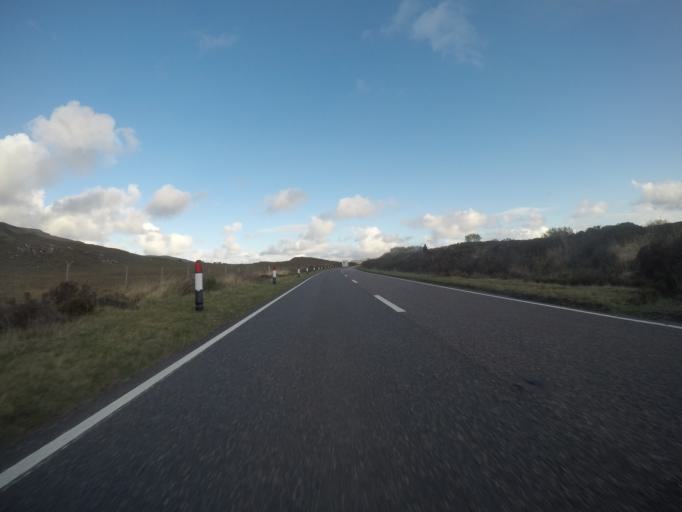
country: GB
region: Scotland
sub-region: Highland
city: Portree
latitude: 57.4651
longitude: -6.2849
